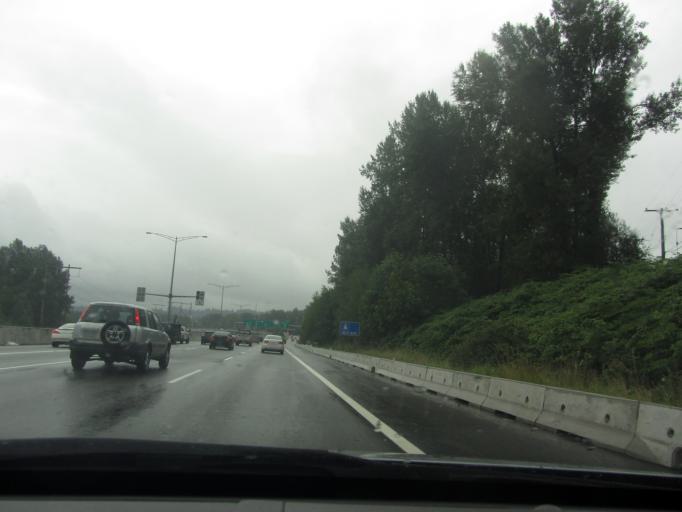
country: CA
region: British Columbia
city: Burnaby
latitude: 49.2476
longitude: -122.9716
